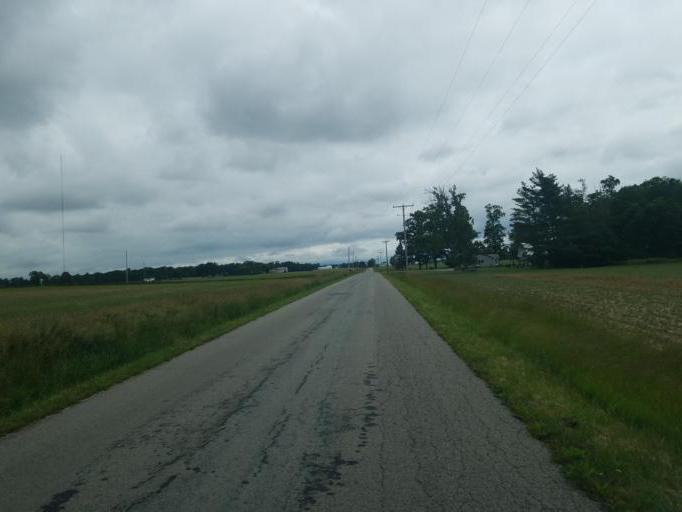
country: US
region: Ohio
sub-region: Crawford County
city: Bucyrus
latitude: 40.7618
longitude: -82.9376
